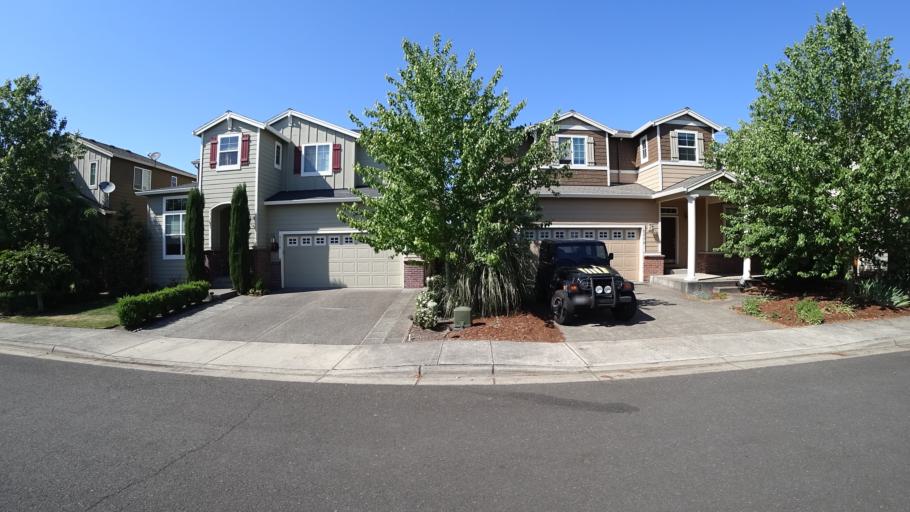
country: US
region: Oregon
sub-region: Washington County
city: Bethany
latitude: 45.5578
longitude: -122.8696
